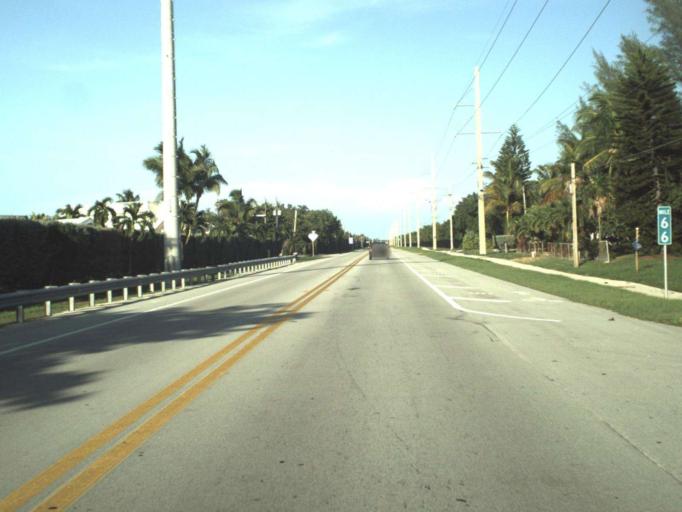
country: US
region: Florida
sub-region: Monroe County
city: Islamorada
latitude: 24.8056
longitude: -80.8435
